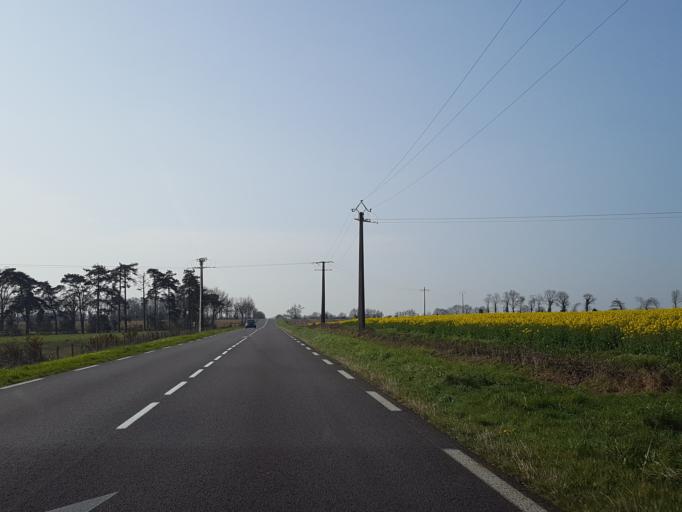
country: FR
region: Pays de la Loire
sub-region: Departement de la Vendee
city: Les Lucs-sur-Boulogne
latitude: 46.8761
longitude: -1.5000
